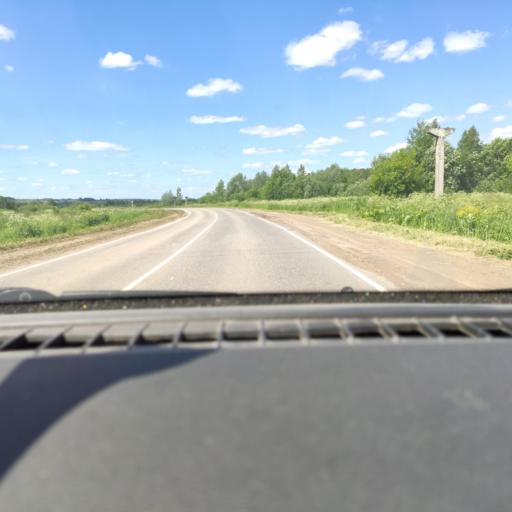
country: RU
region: Perm
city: Chaykovskaya
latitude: 58.0890
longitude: 55.6120
